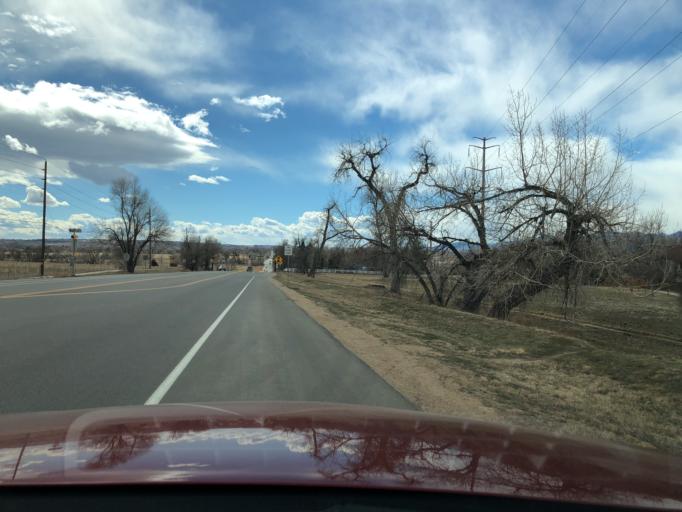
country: US
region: Colorado
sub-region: Boulder County
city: Gunbarrel
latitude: 40.0550
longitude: -105.1784
